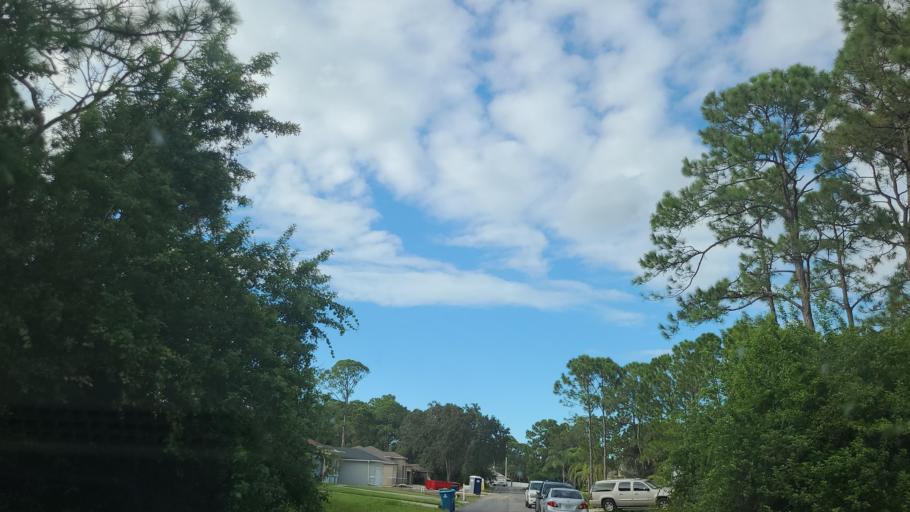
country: US
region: Florida
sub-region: Brevard County
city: June Park
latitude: 27.9978
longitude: -80.6945
